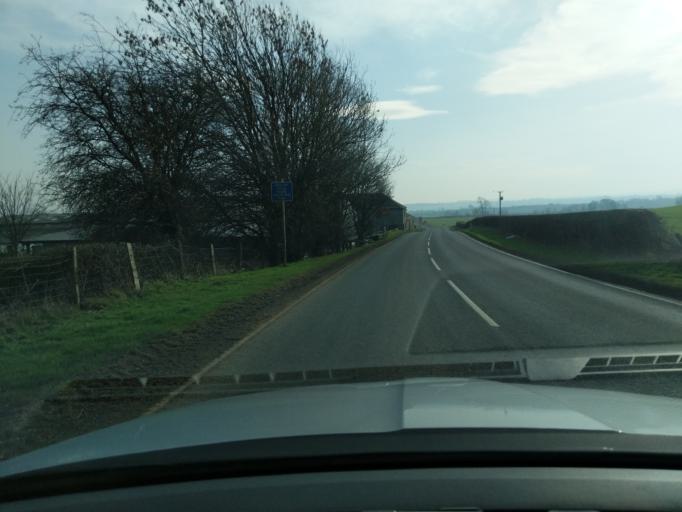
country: GB
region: England
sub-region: North Yorkshire
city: Catterick Garrison
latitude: 54.3370
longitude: -1.6862
